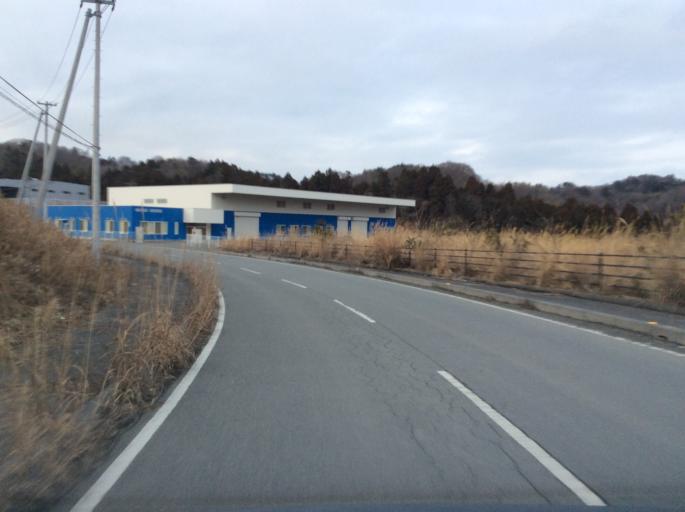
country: JP
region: Fukushima
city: Iwaki
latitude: 37.1249
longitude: 140.9777
